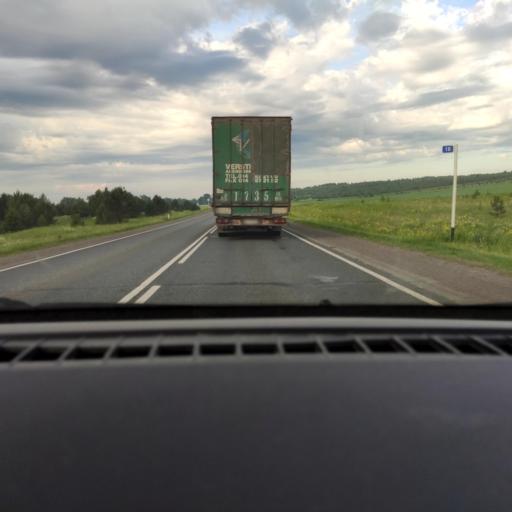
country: RU
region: Udmurtiya
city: Votkinsk
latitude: 57.3684
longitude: 54.4254
